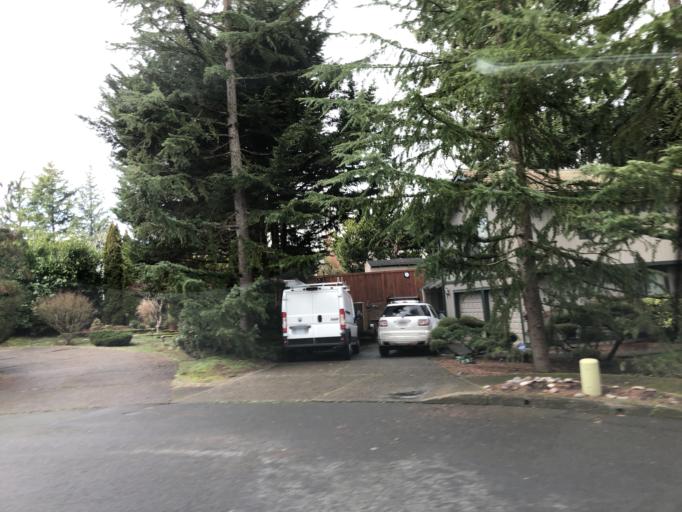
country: US
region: Oregon
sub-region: Washington County
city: Tigard
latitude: 45.4265
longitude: -122.7864
